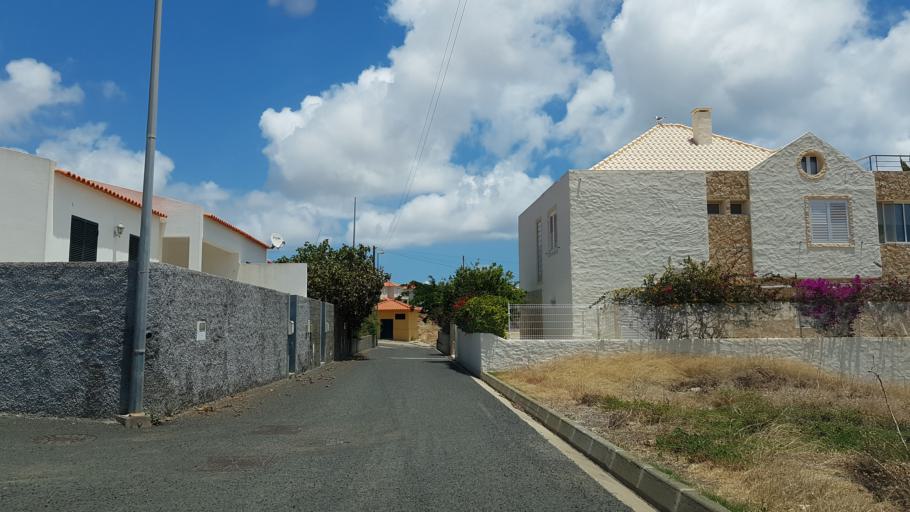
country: PT
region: Madeira
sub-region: Porto Santo
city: Vila de Porto Santo
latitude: 33.0557
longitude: -16.3664
